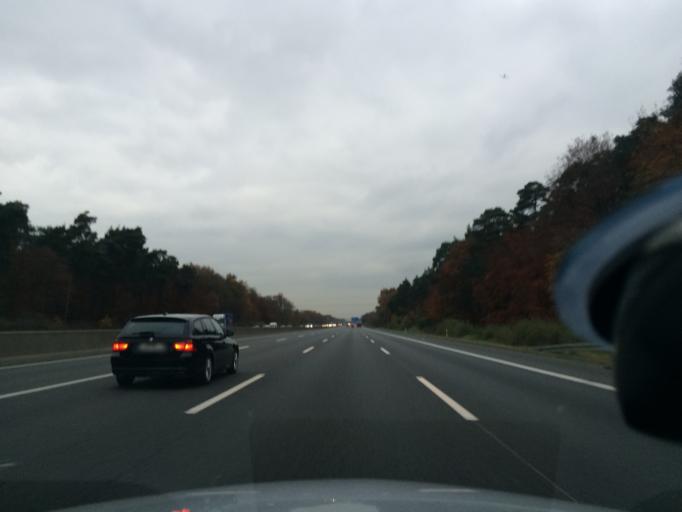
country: DE
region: Hesse
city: Morfelden-Walldorf
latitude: 49.9632
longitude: 8.6063
